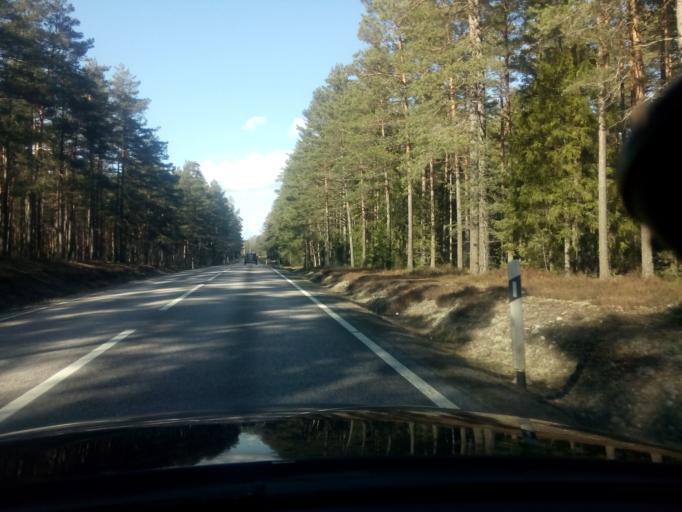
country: SE
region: Soedermanland
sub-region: Strangnas Kommun
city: Akers Styckebruk
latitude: 59.2431
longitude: 16.9394
